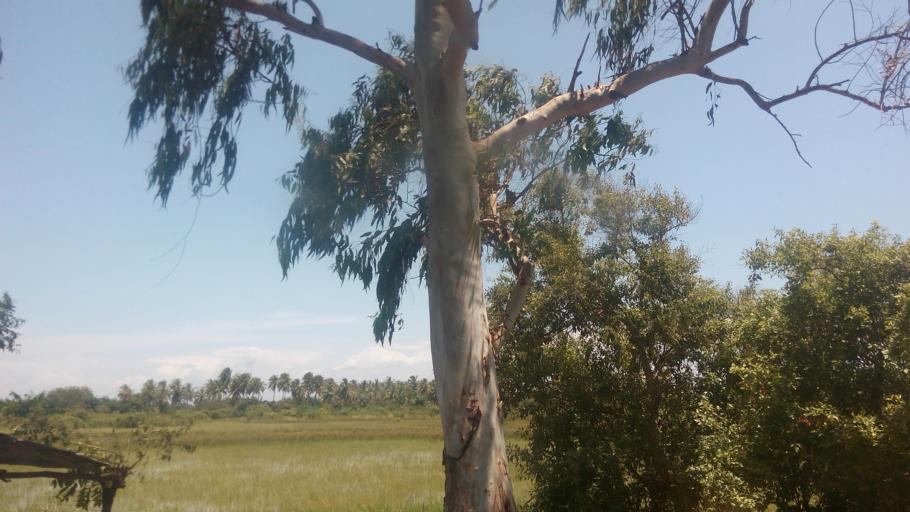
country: BJ
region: Mono
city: Grand-Popo
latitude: 6.2938
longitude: 1.8190
